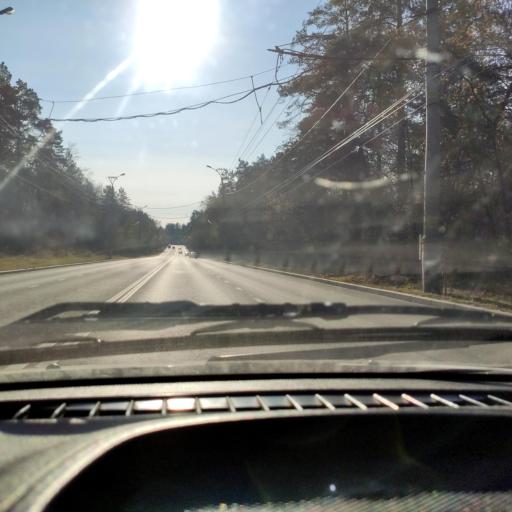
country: RU
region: Samara
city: Zhigulevsk
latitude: 53.4929
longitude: 49.4628
